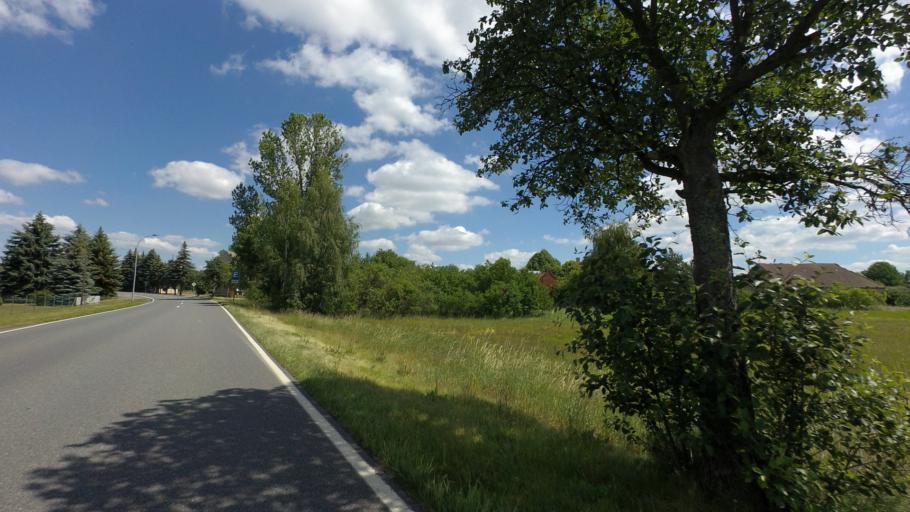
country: DE
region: Brandenburg
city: Luckau
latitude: 51.7725
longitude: 13.6876
